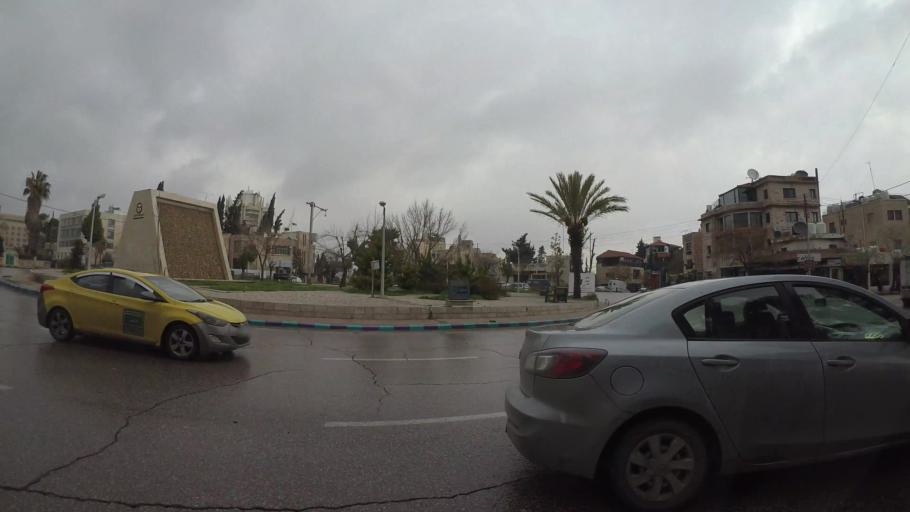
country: JO
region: Amman
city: Amman
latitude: 31.9512
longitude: 35.9158
